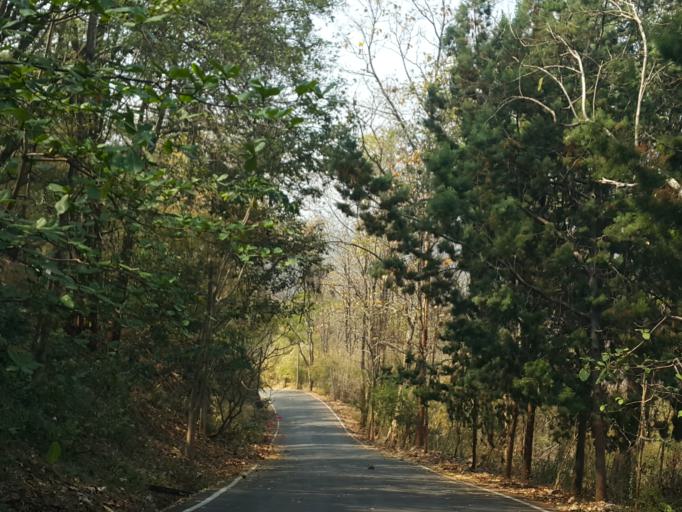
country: TH
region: Chiang Mai
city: Mae On
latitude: 18.7842
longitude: 99.2378
